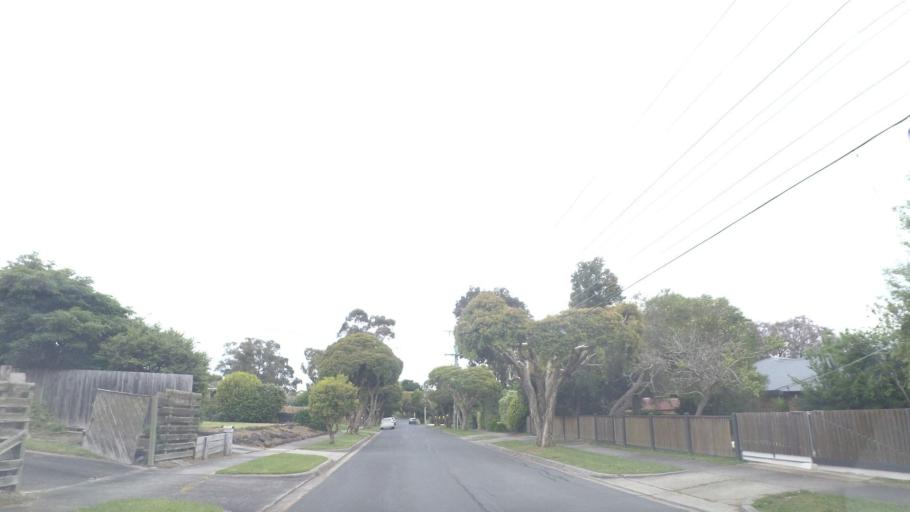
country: AU
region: Victoria
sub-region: Maroondah
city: Croydon South
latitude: -37.8129
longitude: 145.2825
